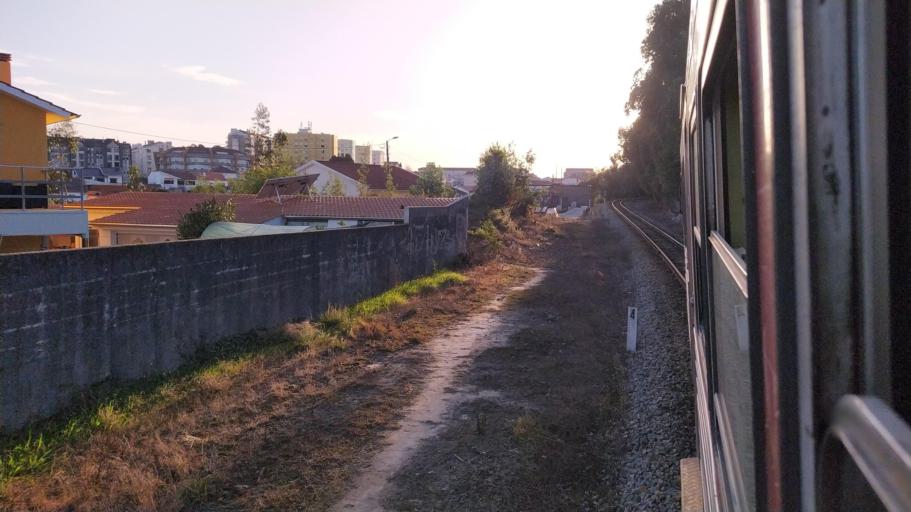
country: PT
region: Aveiro
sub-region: Aveiro
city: Eixo
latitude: 40.6399
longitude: -8.5942
